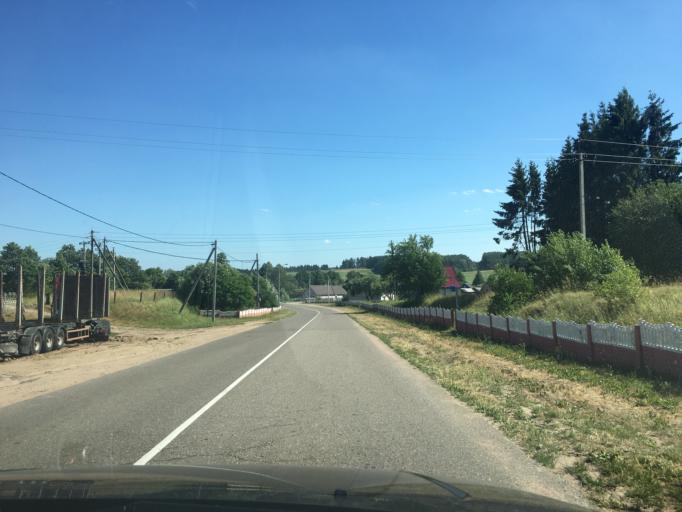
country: BY
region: Grodnenskaya
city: Hal'shany
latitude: 54.2614
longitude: 25.9956
